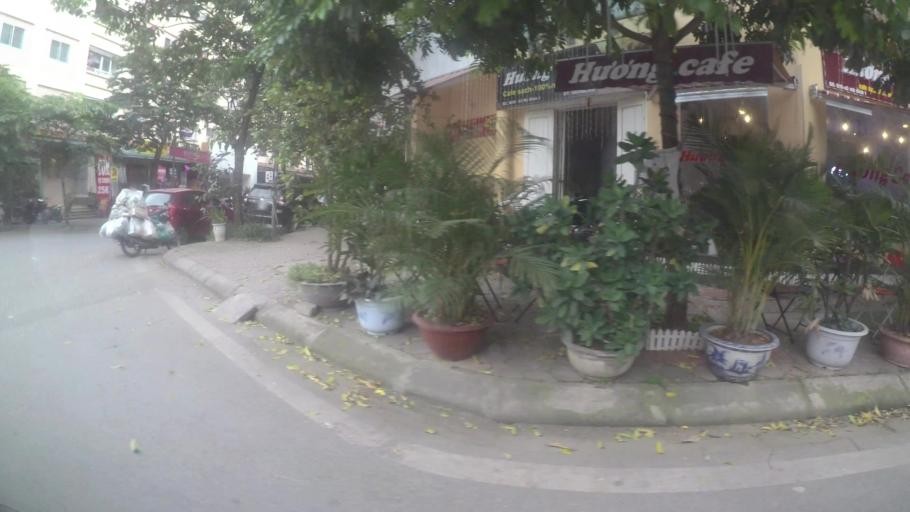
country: VN
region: Ha Noi
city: Cau Dien
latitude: 21.0313
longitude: 105.7623
